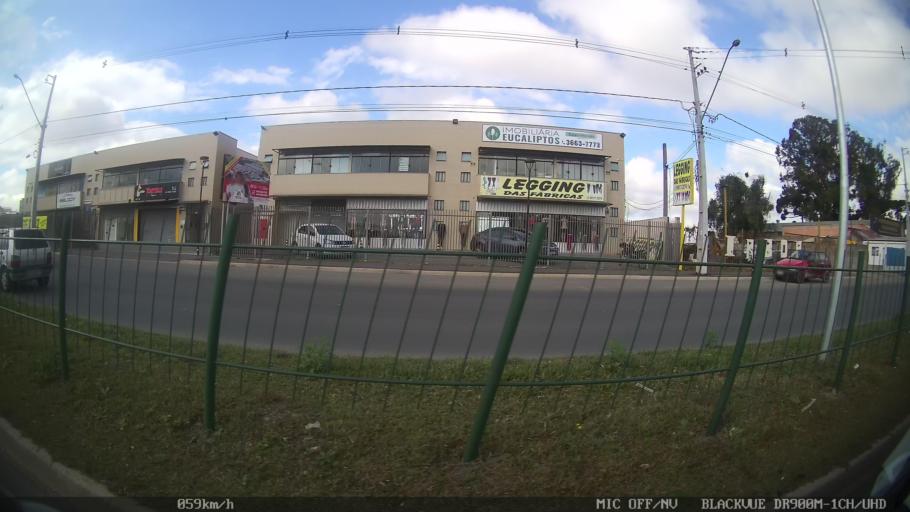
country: BR
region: Parana
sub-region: Pinhais
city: Pinhais
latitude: -25.3721
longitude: -49.1864
